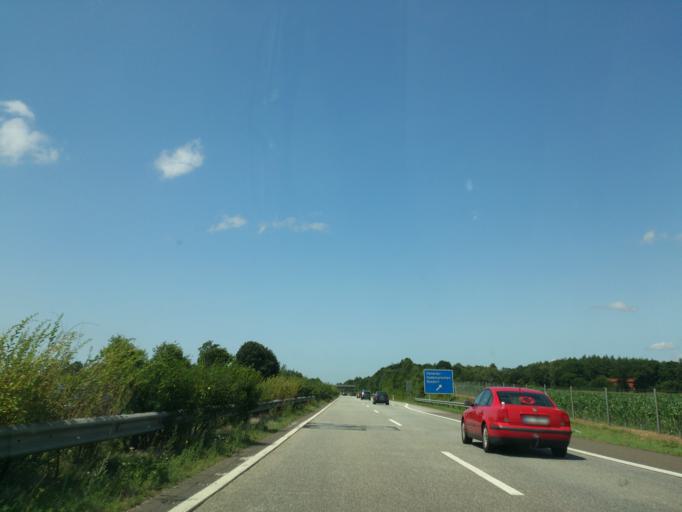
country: DE
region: Schleswig-Holstein
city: Besdorf
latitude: 54.0571
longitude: 9.3706
